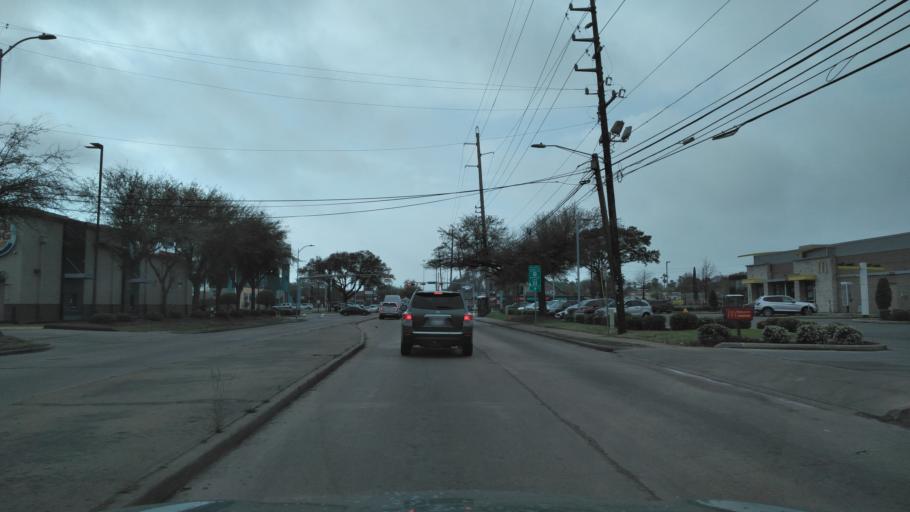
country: US
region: Texas
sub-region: Harris County
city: Bellaire
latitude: 29.7326
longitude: -95.4843
